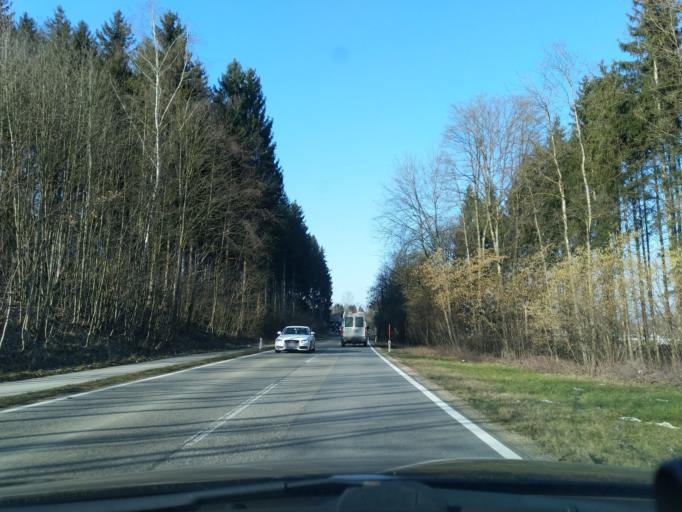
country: AT
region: Upper Austria
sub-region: Politischer Bezirk Ried im Innkreis
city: Ried im Innkreis
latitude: 48.2402
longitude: 13.4599
